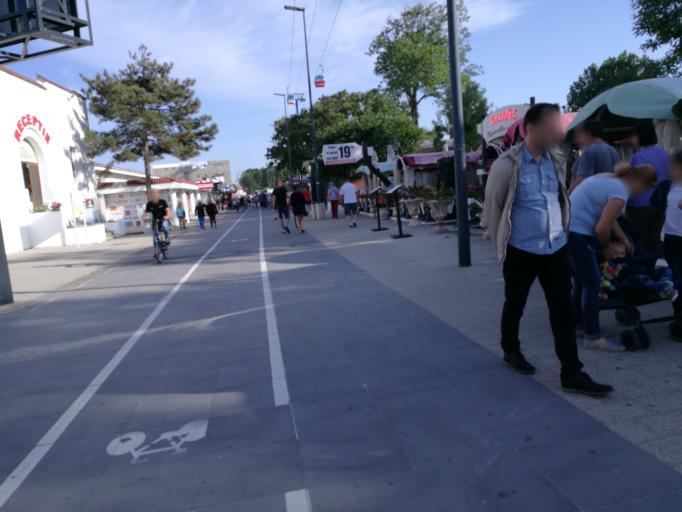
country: RO
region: Constanta
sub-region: Municipiul Constanta
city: Palazu Mare
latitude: 44.2350
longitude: 28.6258
